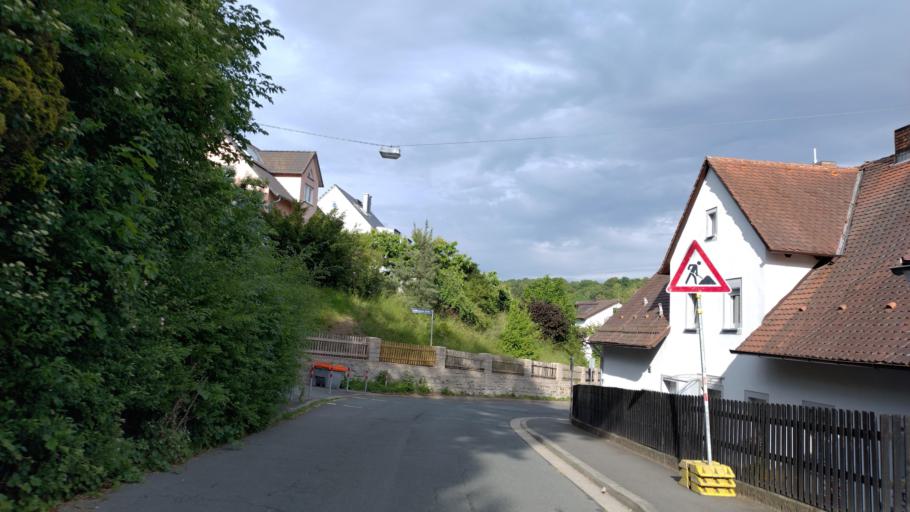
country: DE
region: Bavaria
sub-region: Upper Franconia
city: Bindlach
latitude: 49.9594
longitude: 11.6205
